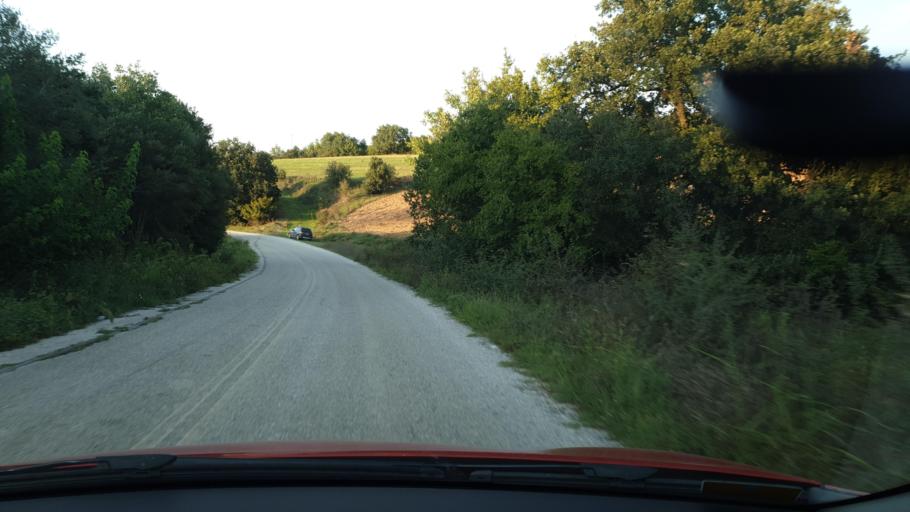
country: GR
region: Central Macedonia
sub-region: Nomos Thessalonikis
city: Nea Apollonia
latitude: 40.5508
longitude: 23.4511
